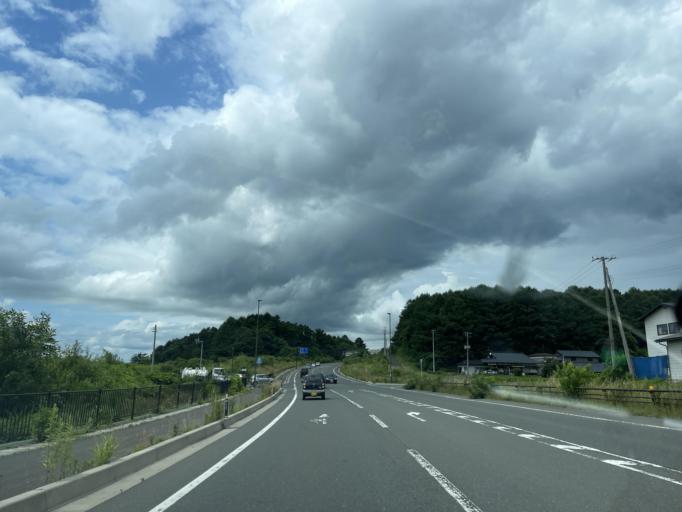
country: JP
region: Iwate
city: Morioka-shi
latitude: 39.8510
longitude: 141.1746
